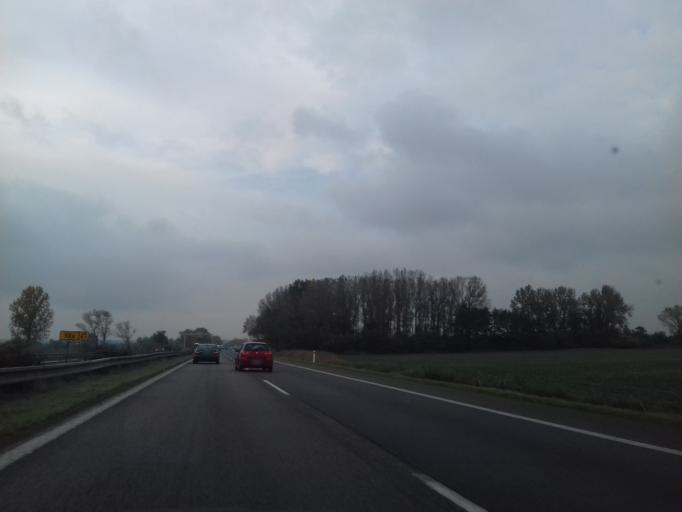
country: SK
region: Bratislavsky
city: Stupava
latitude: 48.2210
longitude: 17.0292
